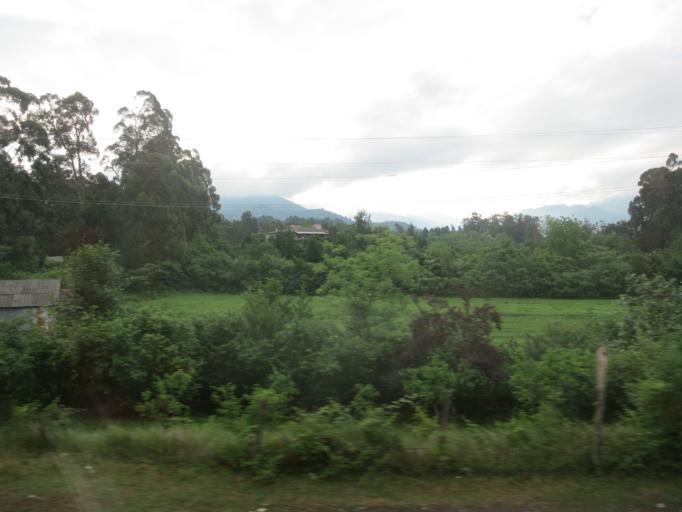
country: GE
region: Ajaria
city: Makhinjauri
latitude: 41.7236
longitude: 41.7296
